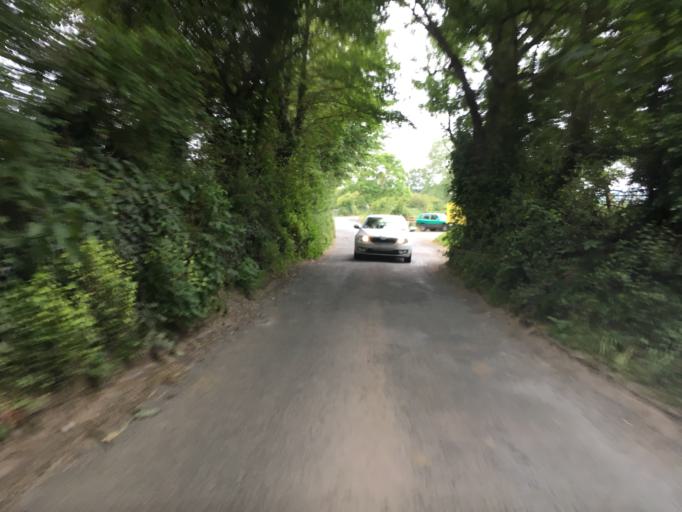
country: GB
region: England
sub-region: North Somerset
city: Yatton
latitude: 51.4190
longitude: -2.8020
